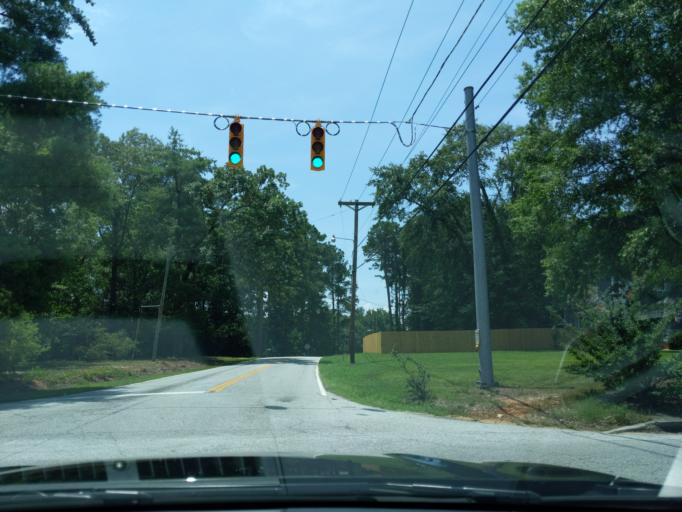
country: US
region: South Carolina
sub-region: Laurens County
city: Laurens
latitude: 34.4882
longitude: -82.0218
